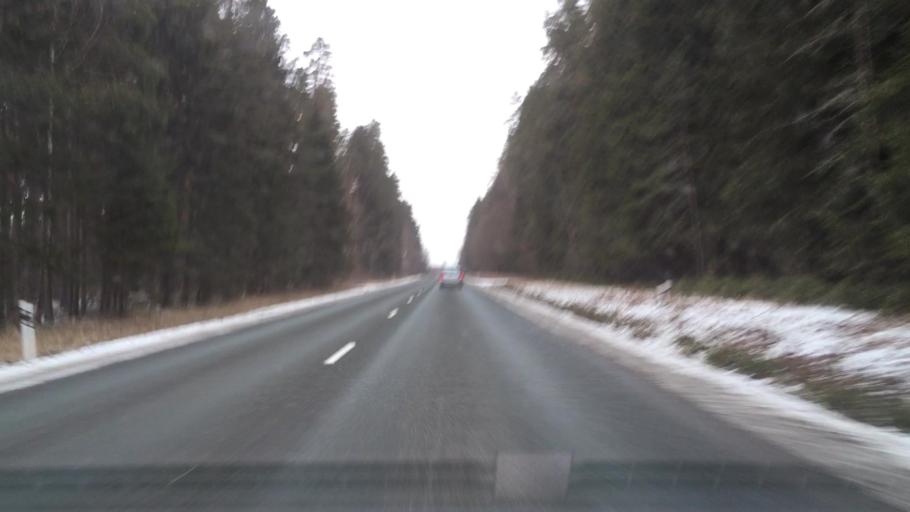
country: LV
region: Valmieras Rajons
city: Valmiera
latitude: 57.5034
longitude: 25.4198
